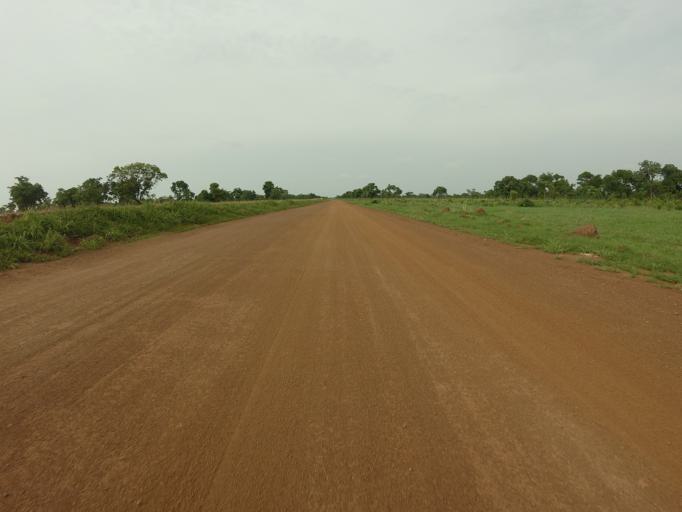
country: GH
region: Northern
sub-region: Yendi
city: Yendi
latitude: 9.7885
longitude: -0.1159
